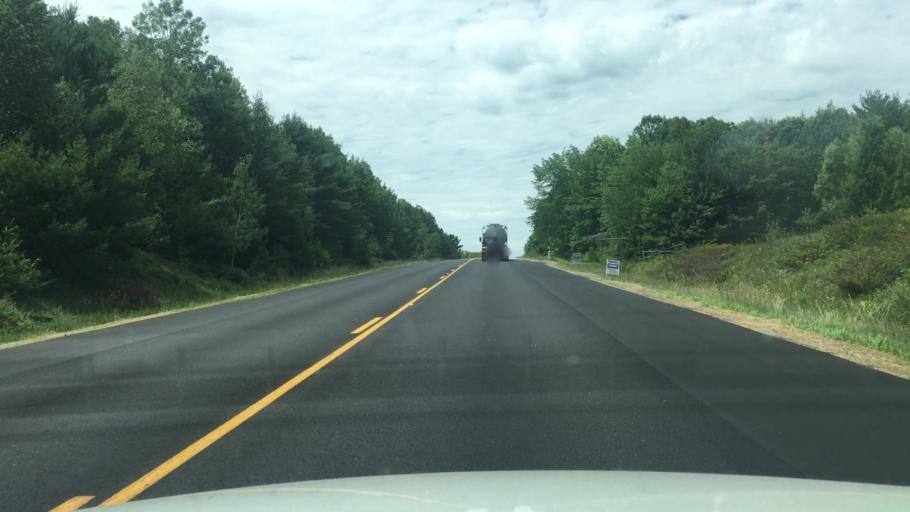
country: US
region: Maine
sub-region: Waldo County
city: Palermo
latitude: 44.3803
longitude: -69.4098
